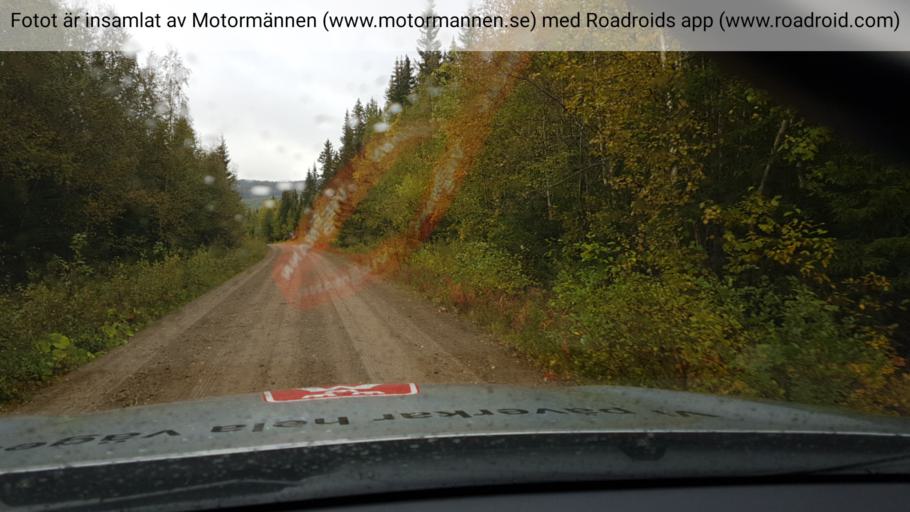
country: SE
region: Jaemtland
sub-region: Harjedalens Kommun
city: Sveg
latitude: 62.2458
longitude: 13.3042
